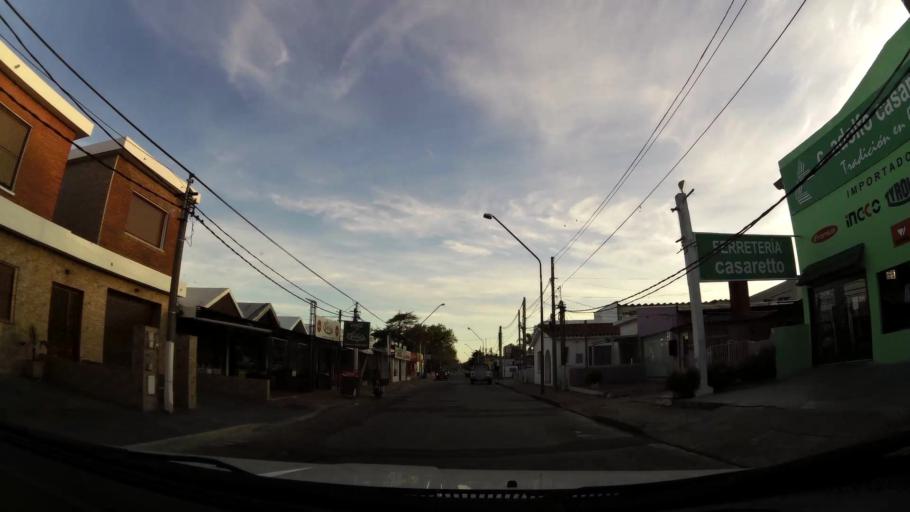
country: UY
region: Maldonado
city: Maldonado
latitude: -34.9111
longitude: -54.9532
